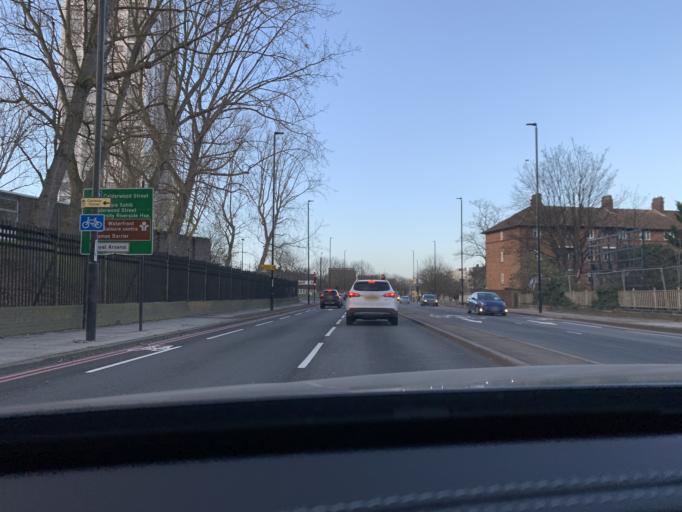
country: GB
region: England
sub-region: Greater London
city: Woolwich
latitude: 51.4877
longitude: 0.0632
